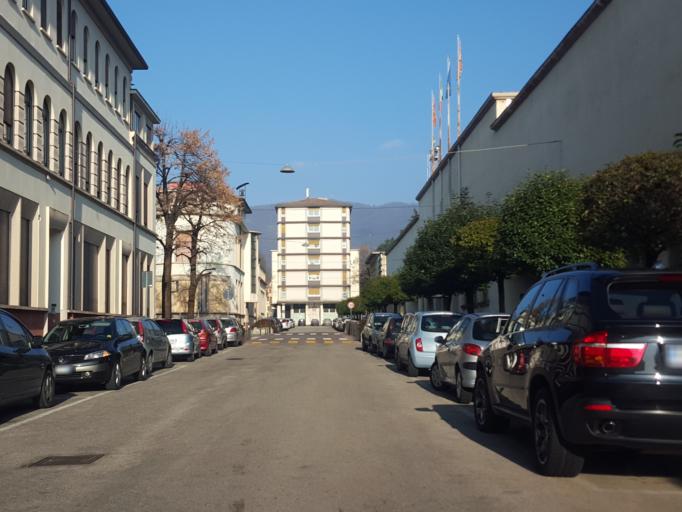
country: IT
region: Veneto
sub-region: Provincia di Vicenza
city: Valdagno
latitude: 45.6482
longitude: 11.3039
